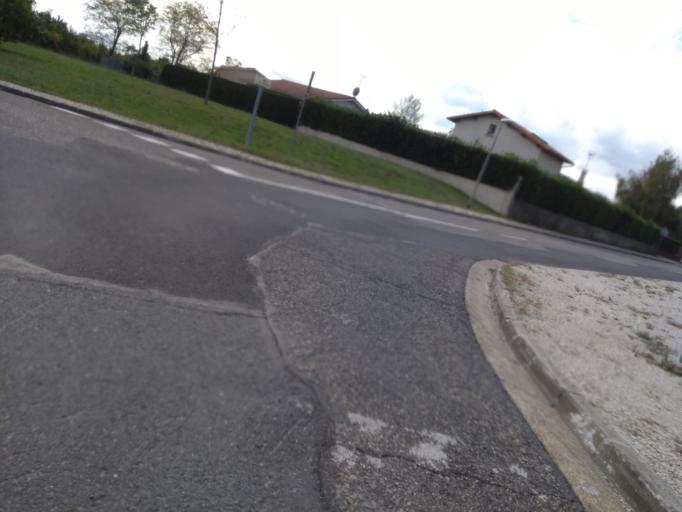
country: FR
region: Aquitaine
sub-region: Departement de la Gironde
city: Canejan
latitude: 44.7663
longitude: -0.6607
